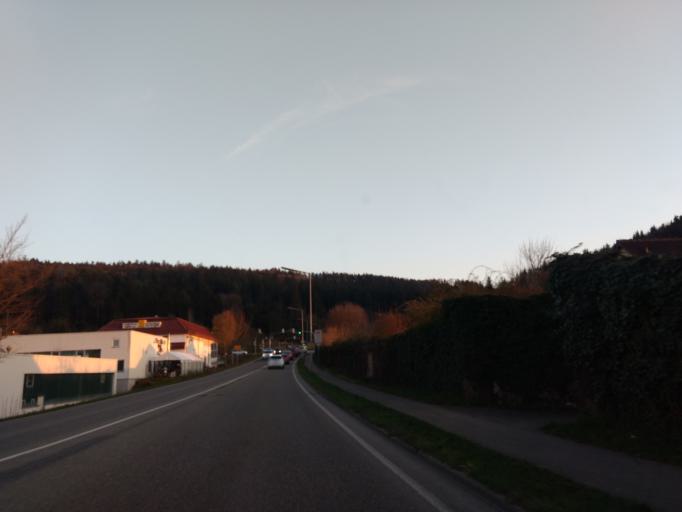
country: DE
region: Baden-Wuerttemberg
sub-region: Regierungsbezirk Stuttgart
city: Lorch
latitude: 48.7951
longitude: 9.7029
